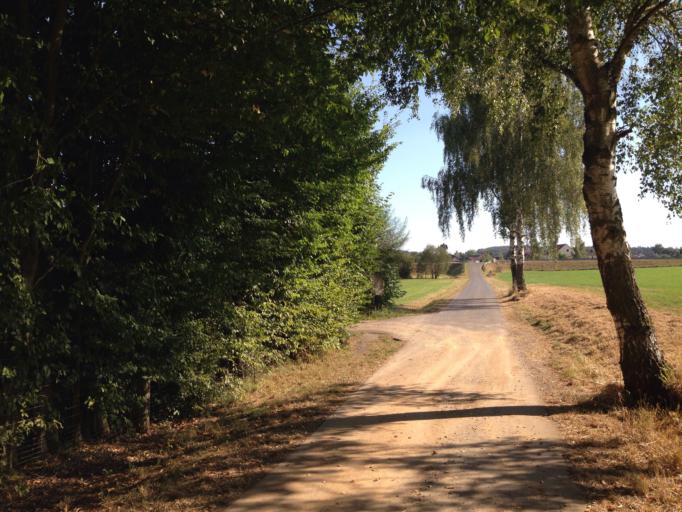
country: DE
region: Hesse
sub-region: Regierungsbezirk Giessen
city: Rabenau
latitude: 50.6529
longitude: 8.8937
